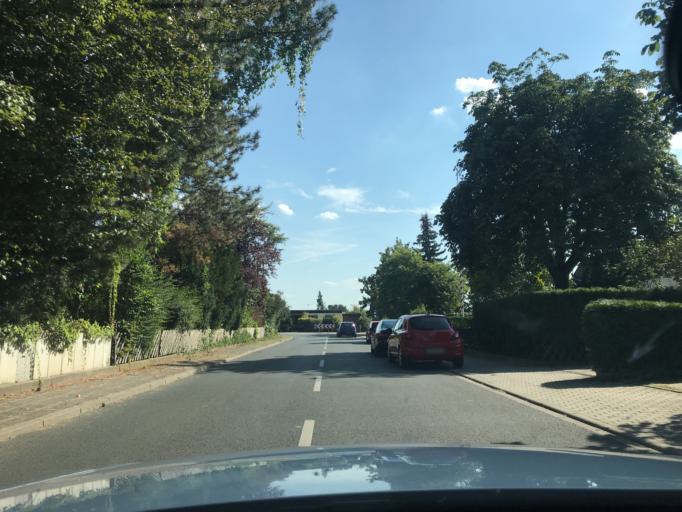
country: DE
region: Bavaria
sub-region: Regierungsbezirk Mittelfranken
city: Erlangen
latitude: 49.5543
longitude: 11.0164
